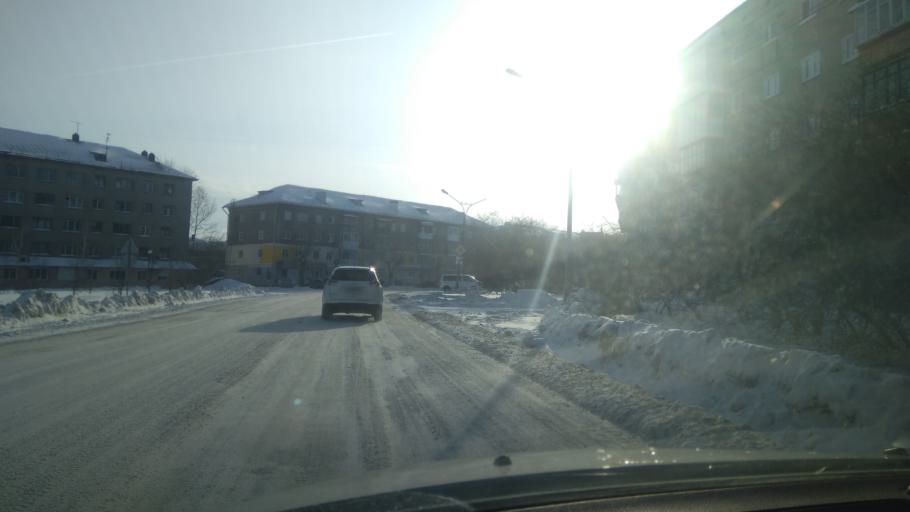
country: RU
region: Sverdlovsk
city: Sukhoy Log
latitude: 56.9090
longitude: 62.0337
